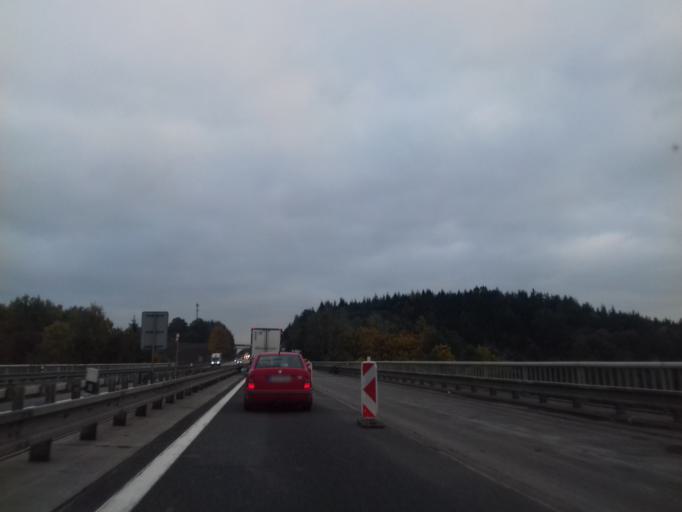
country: CZ
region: Central Bohemia
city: Ondrejov
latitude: 49.8999
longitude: 14.7403
